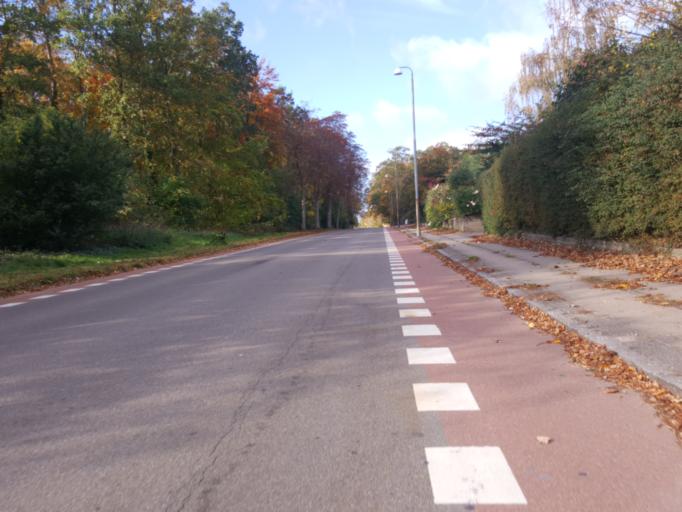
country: DK
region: Zealand
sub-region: Kalundborg Kommune
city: Kalundborg
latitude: 55.6894
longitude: 11.0760
